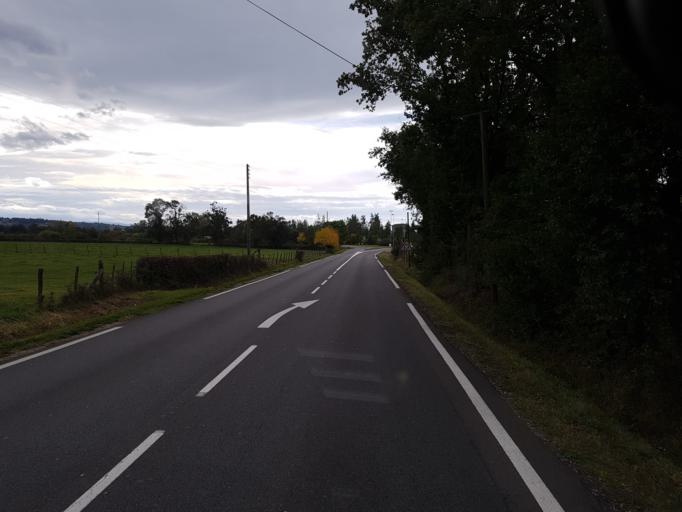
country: FR
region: Rhone-Alpes
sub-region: Departement de la Loire
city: Chamboeuf
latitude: 45.5759
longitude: 4.3041
